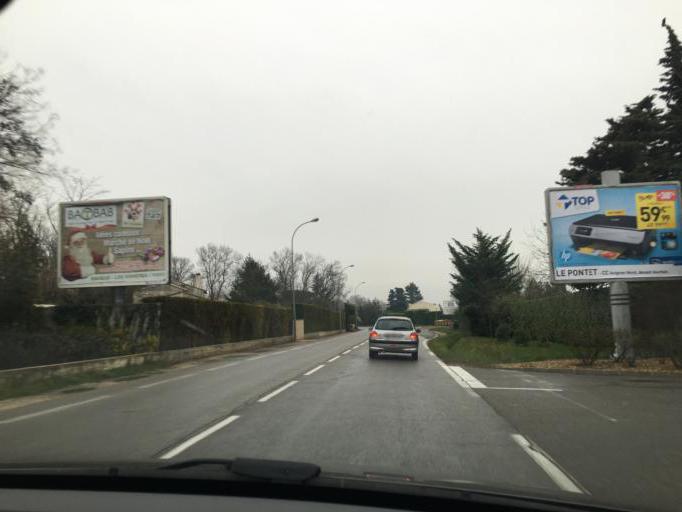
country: FR
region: Provence-Alpes-Cote d'Azur
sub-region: Departement du Vaucluse
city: L'Isle-sur-la-Sorgue
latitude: 43.9163
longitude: 5.0658
